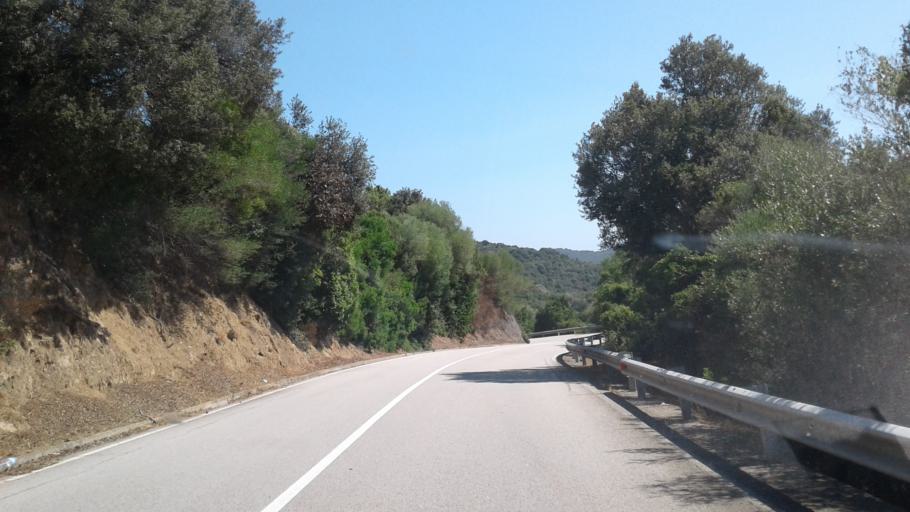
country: IT
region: Sardinia
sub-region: Provincia di Olbia-Tempio
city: Palau
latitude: 41.1345
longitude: 9.3008
